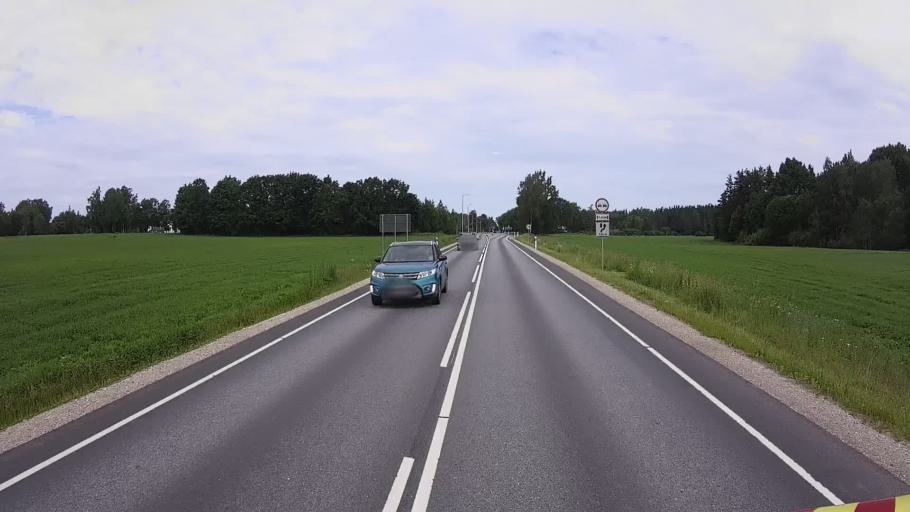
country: EE
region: Viljandimaa
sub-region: Viljandi linn
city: Viljandi
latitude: 58.2385
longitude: 25.5962
